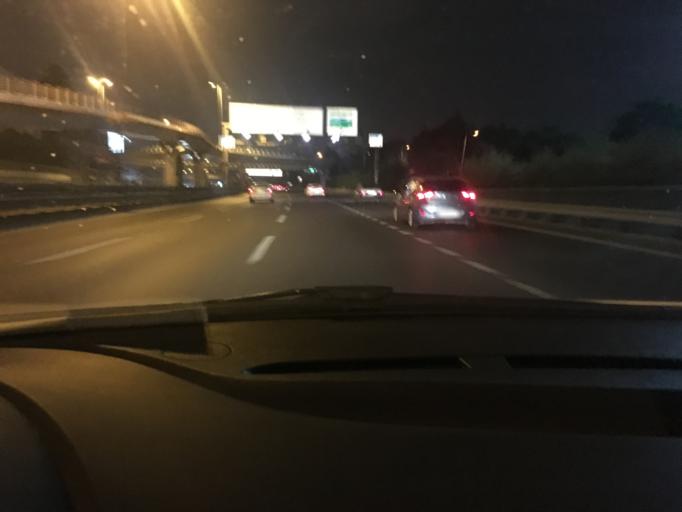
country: TR
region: Istanbul
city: Zeytinburnu
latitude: 41.0211
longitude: 28.9188
